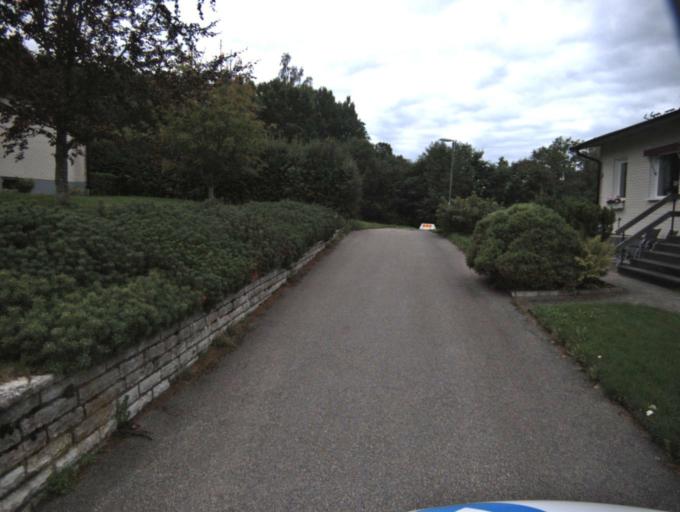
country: SE
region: Vaestra Goetaland
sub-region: Ulricehamns Kommun
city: Ulricehamn
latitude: 57.7960
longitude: 13.4273
